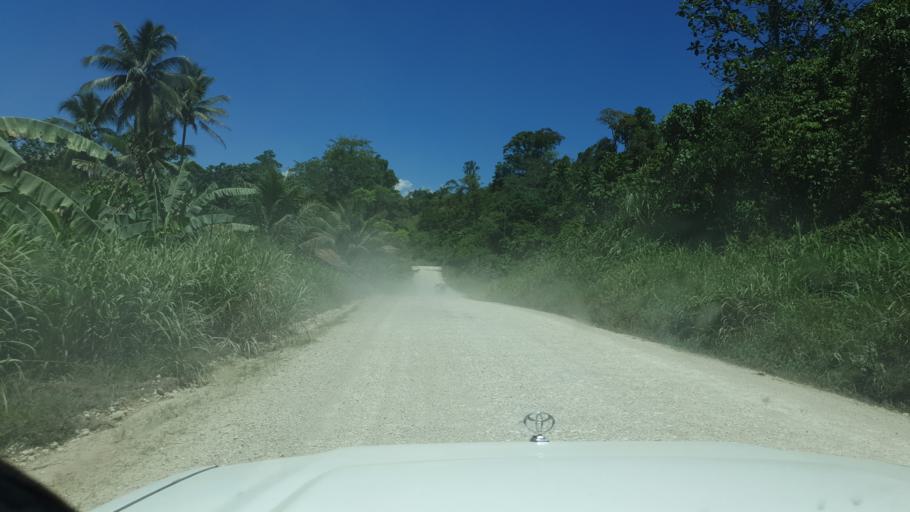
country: PG
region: Madang
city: Madang
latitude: -5.5370
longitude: 145.4070
